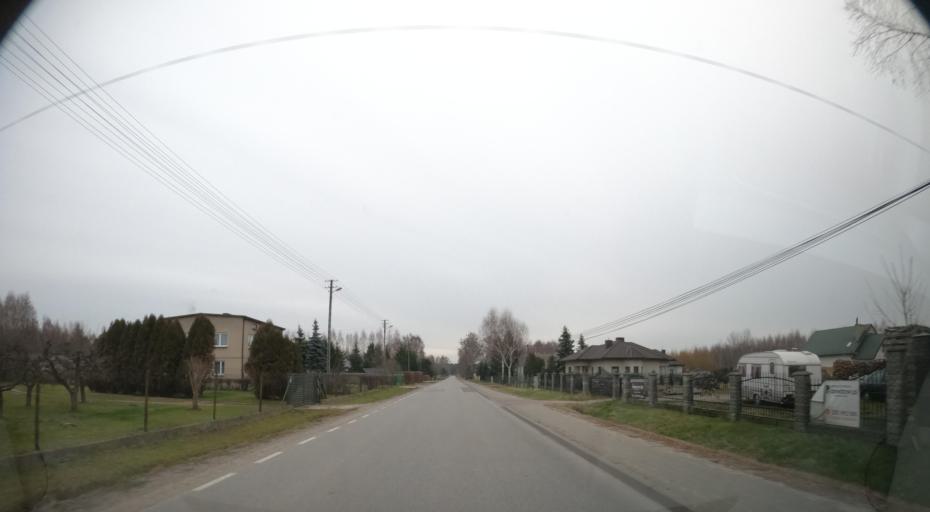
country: PL
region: Masovian Voivodeship
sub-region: Powiat radomski
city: Jedlinsk
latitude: 51.4896
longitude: 21.1362
